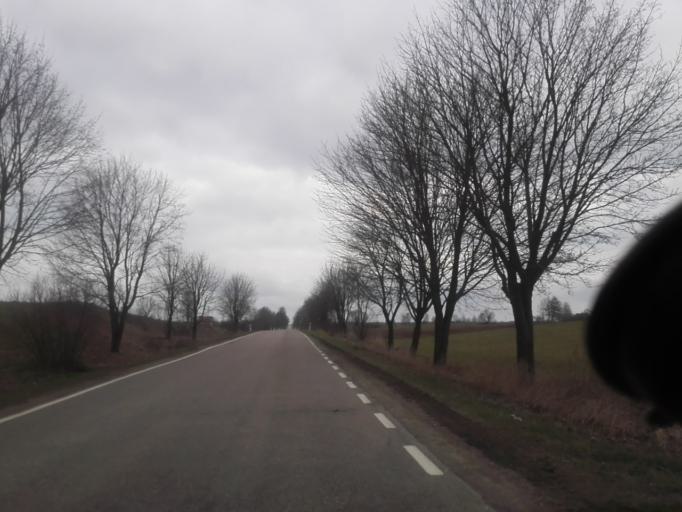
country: PL
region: Podlasie
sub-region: Suwalki
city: Suwalki
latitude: 54.2386
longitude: 22.9154
